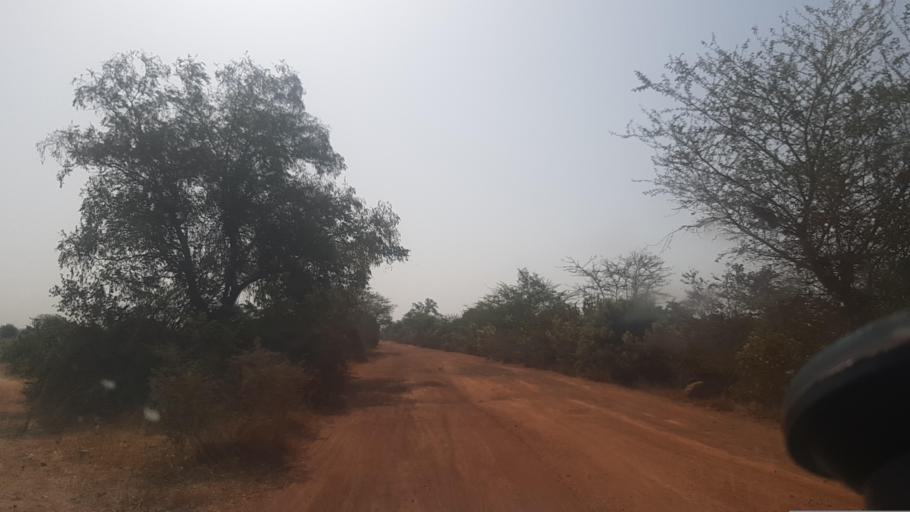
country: ML
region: Segou
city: Baroueli
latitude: 13.1394
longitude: -6.5127
